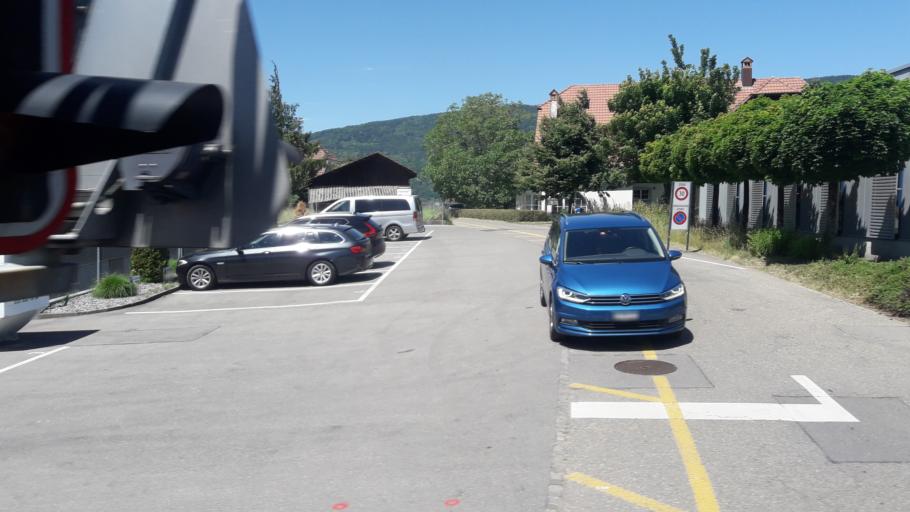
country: CH
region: Bern
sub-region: Biel/Bienne District
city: Bellmund
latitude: 47.0979
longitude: 7.2152
